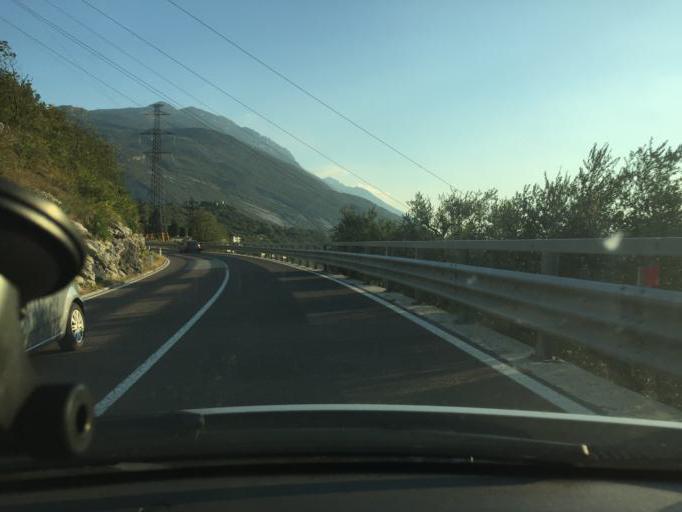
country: IT
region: Trentino-Alto Adige
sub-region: Provincia di Trento
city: Nago-Torbole
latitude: 45.8830
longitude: 10.8858
